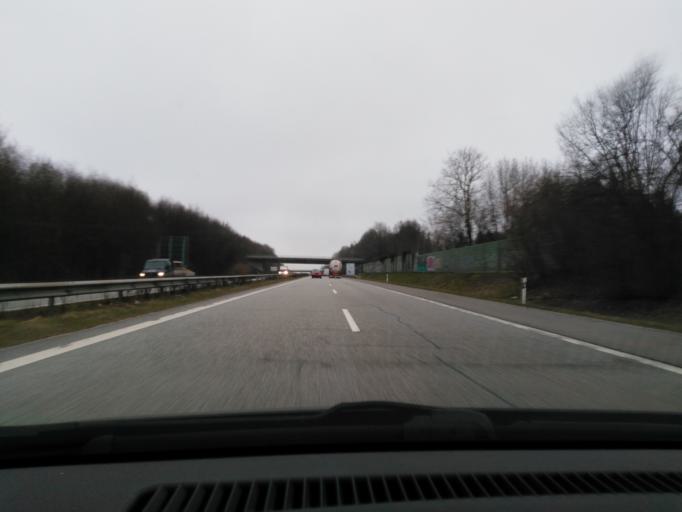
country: DE
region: Schleswig-Holstein
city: Stolpe
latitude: 54.1289
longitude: 10.2174
